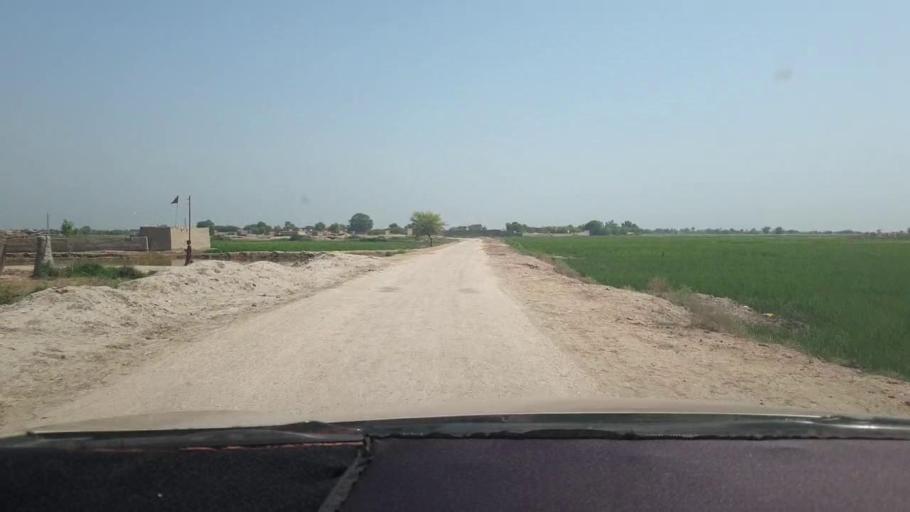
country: PK
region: Sindh
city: Miro Khan
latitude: 27.6740
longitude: 68.0948
